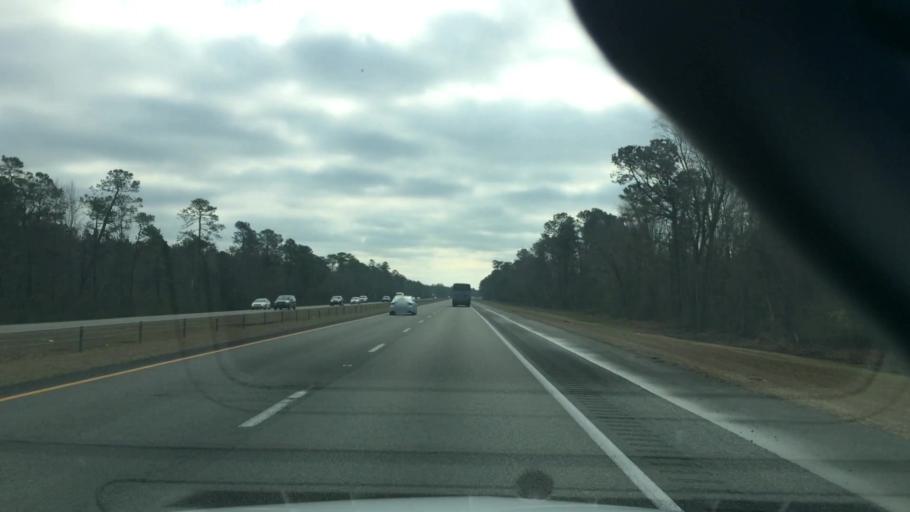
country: US
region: North Carolina
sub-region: Pender County
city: Rocky Point
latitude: 34.4018
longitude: -77.8727
